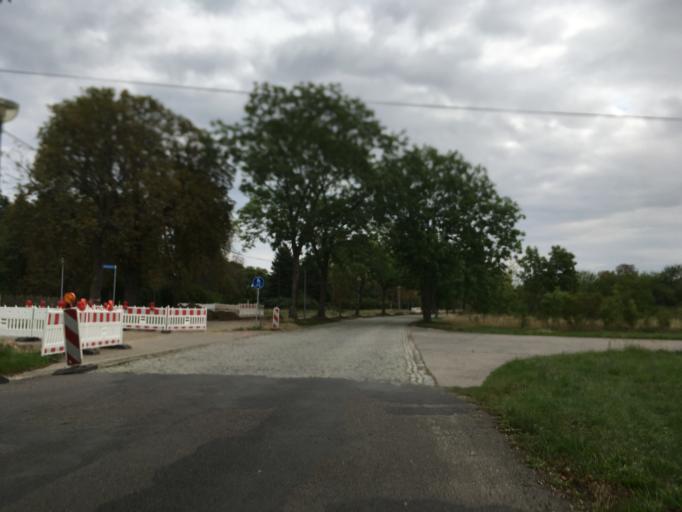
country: DE
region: Brandenburg
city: Schwedt (Oder)
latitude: 53.0703
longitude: 14.2699
